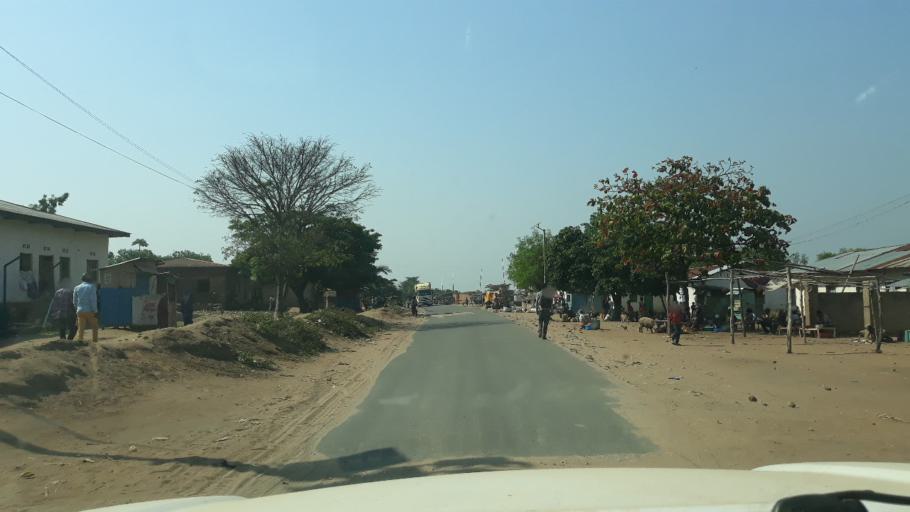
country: CD
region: South Kivu
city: Uvira
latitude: -3.2337
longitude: 29.1652
